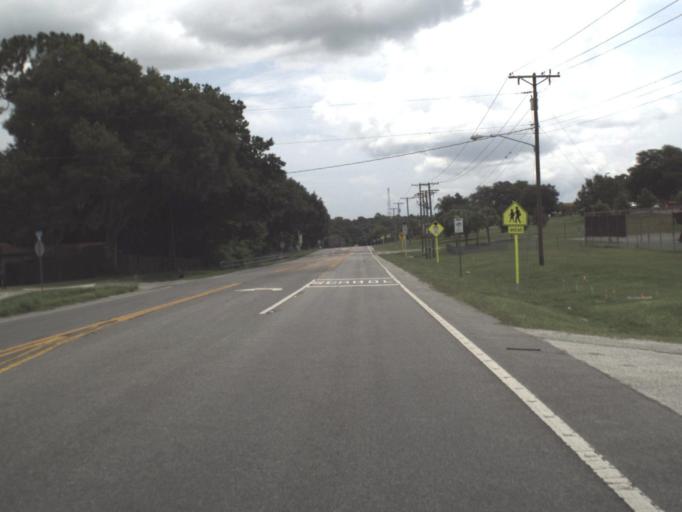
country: US
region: Florida
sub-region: Pasco County
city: Dade City
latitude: 28.3516
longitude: -82.2081
